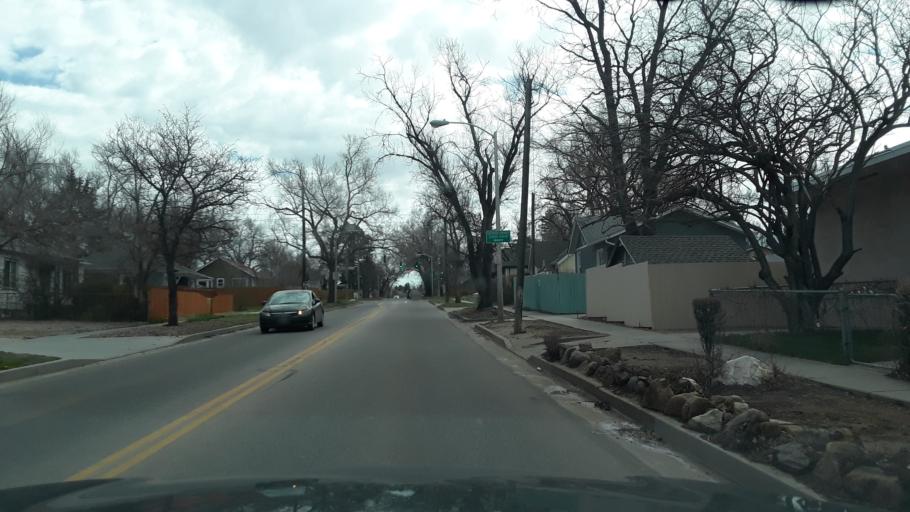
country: US
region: Colorado
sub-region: El Paso County
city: Colorado Springs
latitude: 38.8500
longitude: -104.8043
